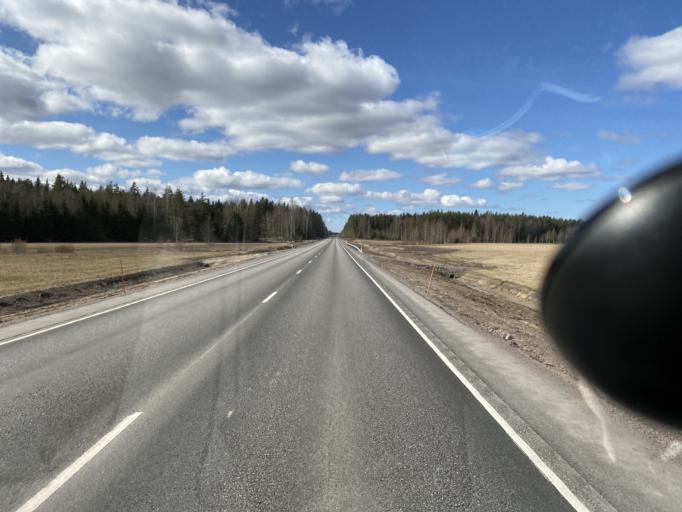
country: FI
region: Satakunta
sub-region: Rauma
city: Koeylioe
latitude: 61.1649
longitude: 22.3605
